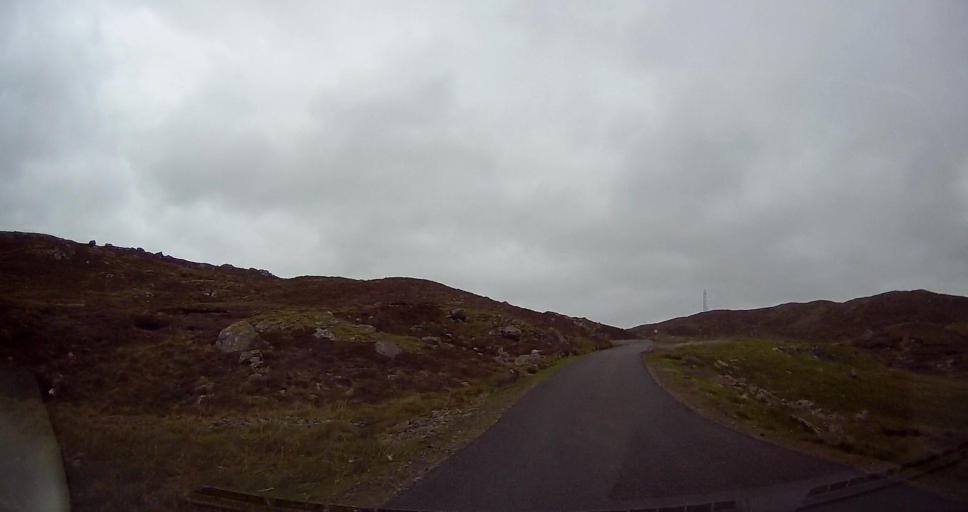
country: GB
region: Scotland
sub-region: Shetland Islands
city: Lerwick
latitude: 60.3411
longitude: -1.3149
